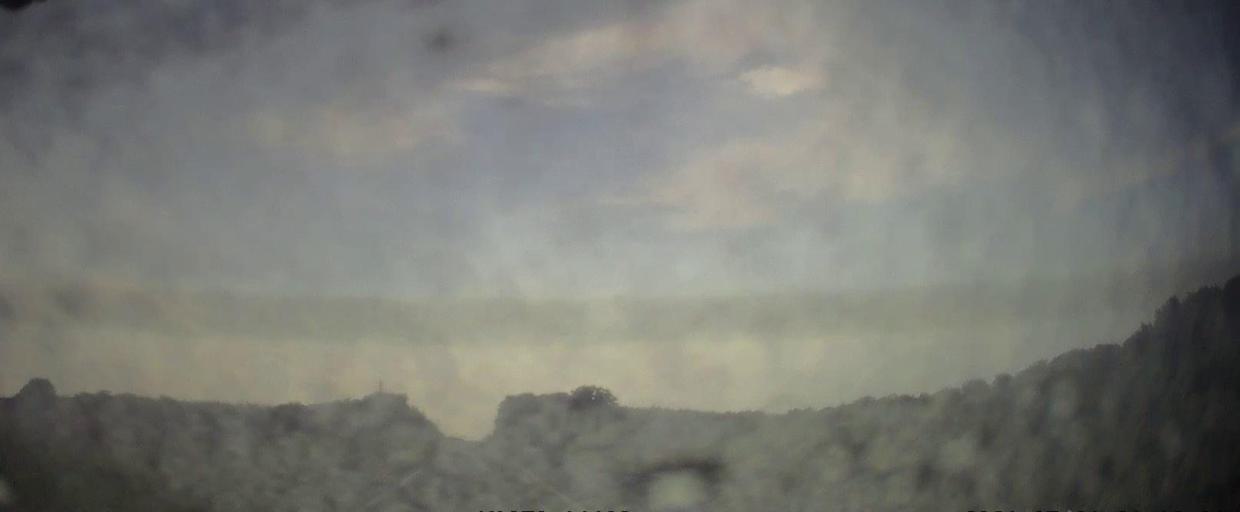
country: US
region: Georgia
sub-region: Dodge County
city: Chester
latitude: 32.5485
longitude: -83.1247
